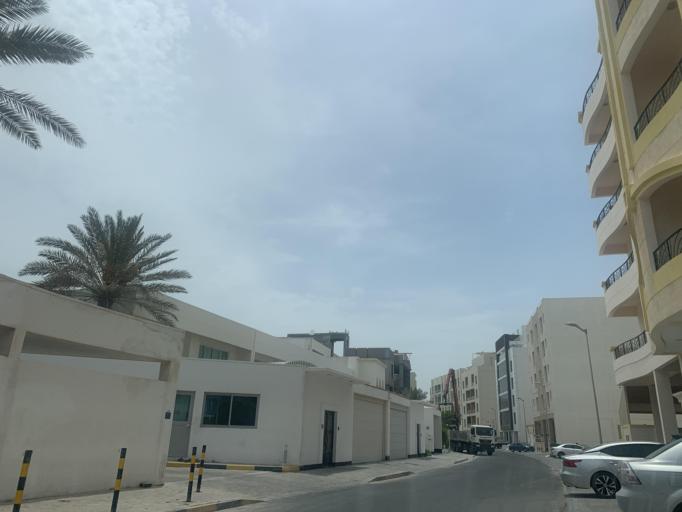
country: BH
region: Muharraq
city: Al Hadd
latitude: 26.2996
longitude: 50.6599
